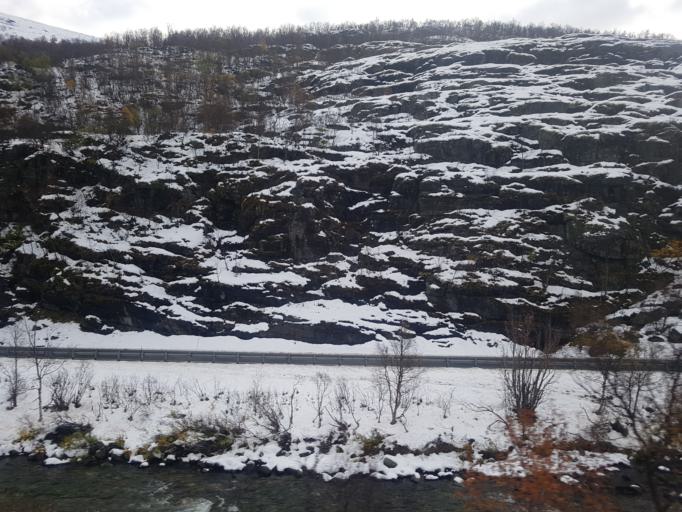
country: NO
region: Sor-Trondelag
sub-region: Oppdal
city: Oppdal
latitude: 62.3326
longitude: 9.6214
